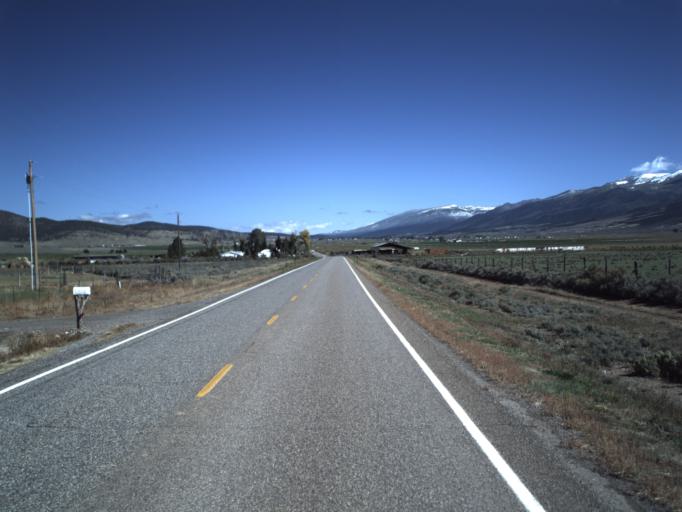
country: US
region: Utah
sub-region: Sevier County
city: Monroe
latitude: 38.4417
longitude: -111.9182
